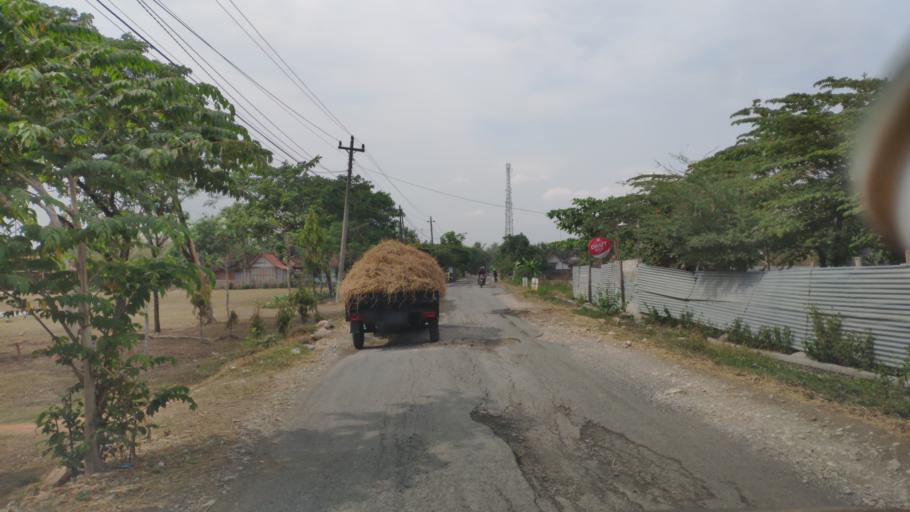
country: ID
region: Central Java
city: Banjarejo
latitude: -7.0305
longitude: 111.3480
